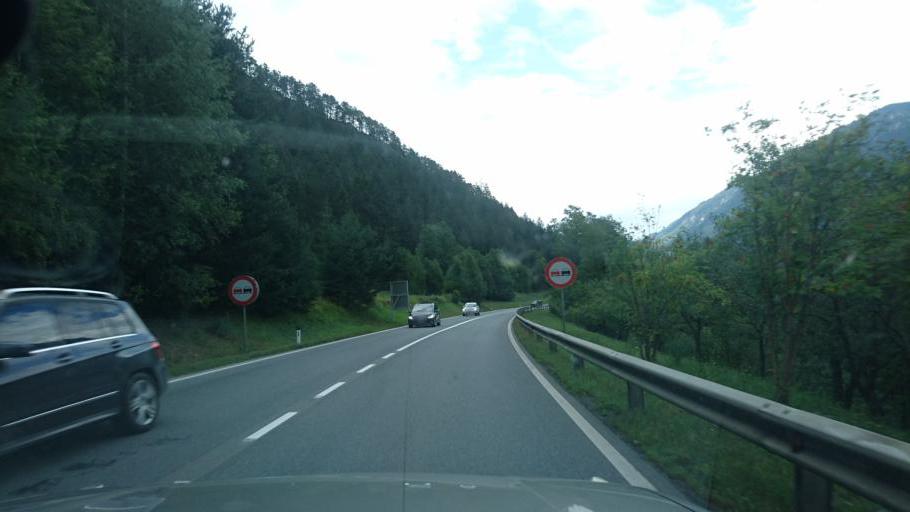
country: AT
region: Tyrol
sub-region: Politischer Bezirk Landeck
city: Pfunds
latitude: 46.9566
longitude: 10.5155
